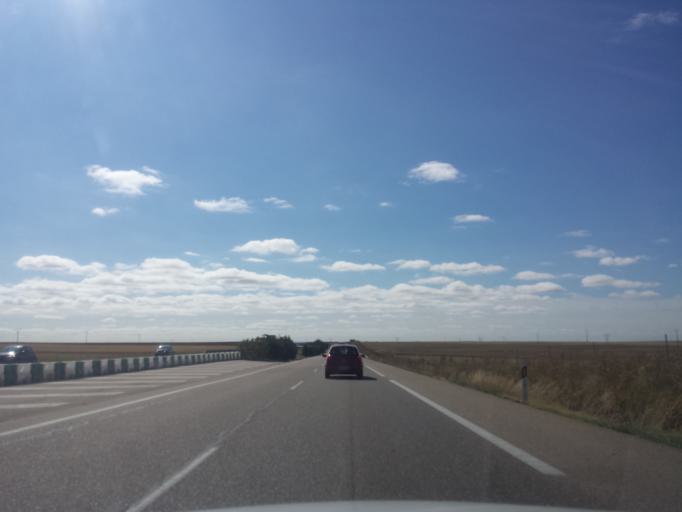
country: ES
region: Castille and Leon
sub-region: Provincia de Zamora
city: San Esteban del Molar
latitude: 41.9305
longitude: -5.5348
